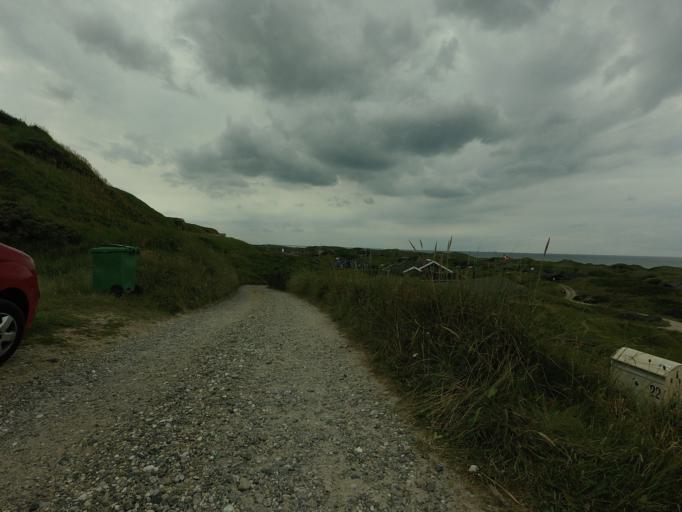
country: DK
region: North Denmark
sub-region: Jammerbugt Kommune
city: Pandrup
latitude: 57.3114
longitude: 9.6512
